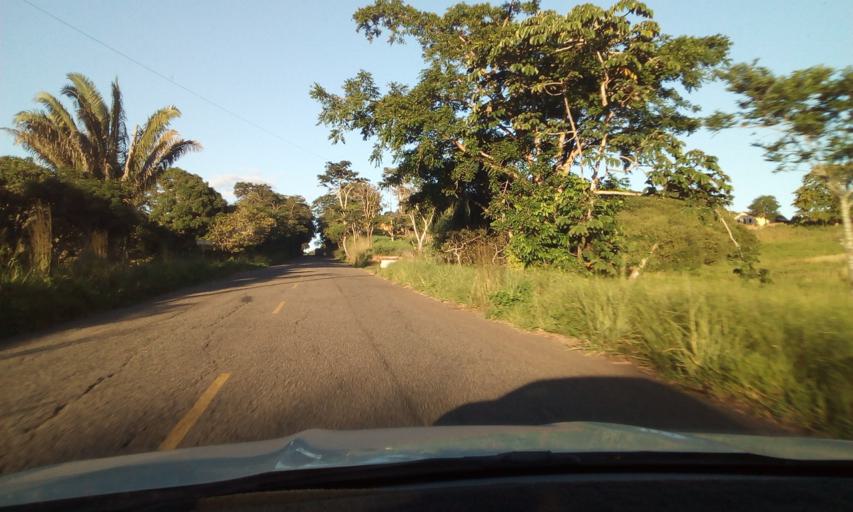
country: BR
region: Paraiba
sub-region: Areia
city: Remigio
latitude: -6.9645
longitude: -35.7645
